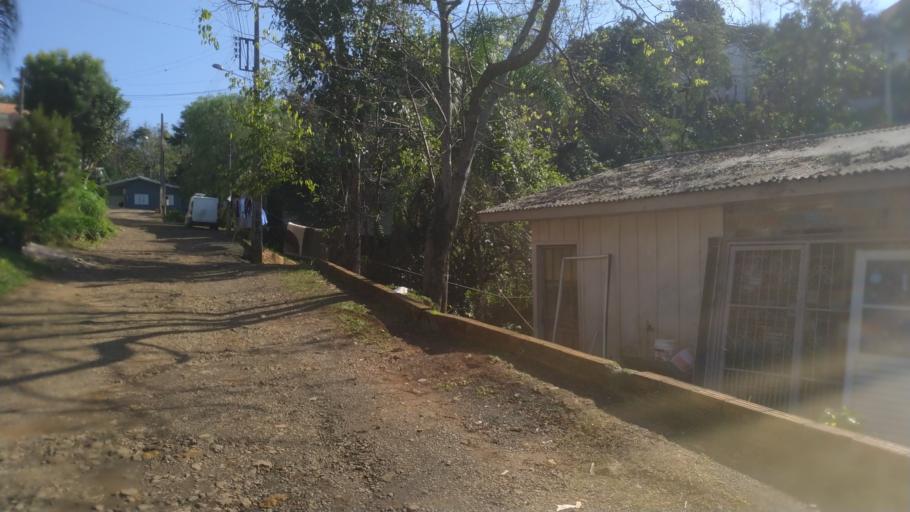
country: BR
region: Santa Catarina
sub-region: Chapeco
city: Chapeco
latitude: -27.1013
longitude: -52.6355
